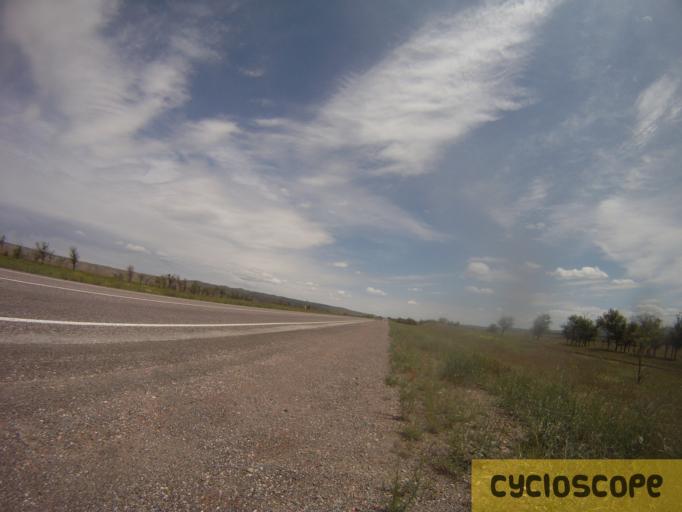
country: KZ
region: Zhambyl
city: Georgiyevka
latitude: 43.3135
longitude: 74.9180
